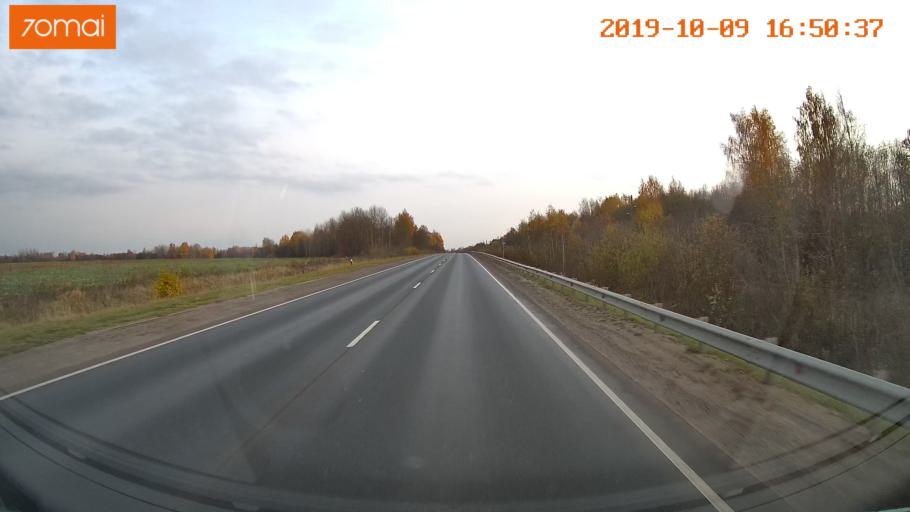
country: RU
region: Kostroma
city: Volgorechensk
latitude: 57.3984
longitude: 41.2112
